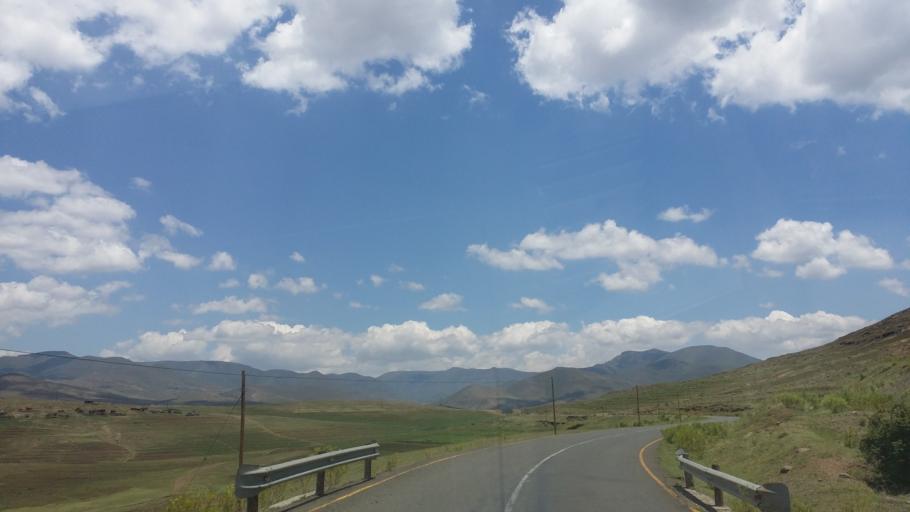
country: LS
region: Mokhotlong
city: Mokhotlong
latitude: -29.2219
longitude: 28.9048
